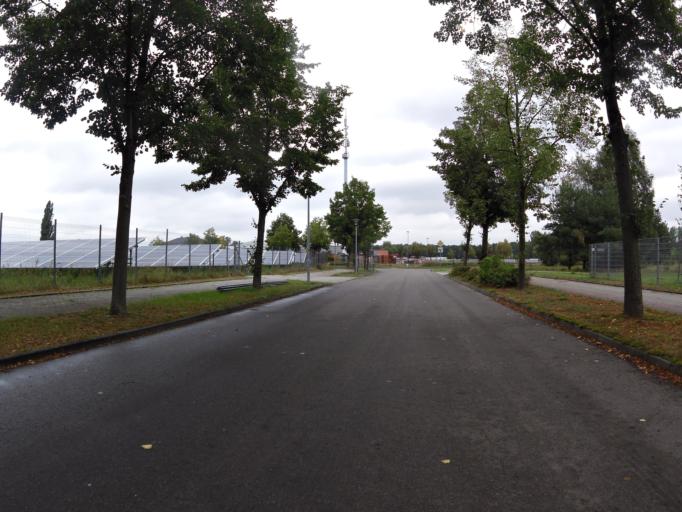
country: DE
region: Brandenburg
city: Storkow
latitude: 52.2665
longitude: 13.9441
